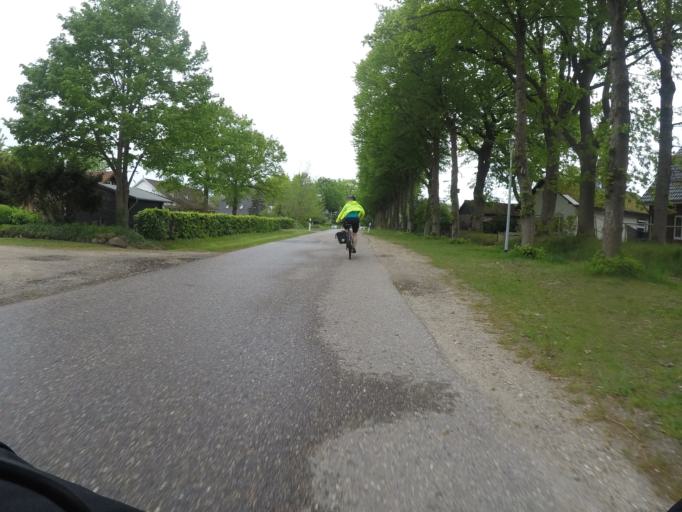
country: DE
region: Schleswig-Holstein
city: Rickling
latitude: 54.0039
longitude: 10.1596
